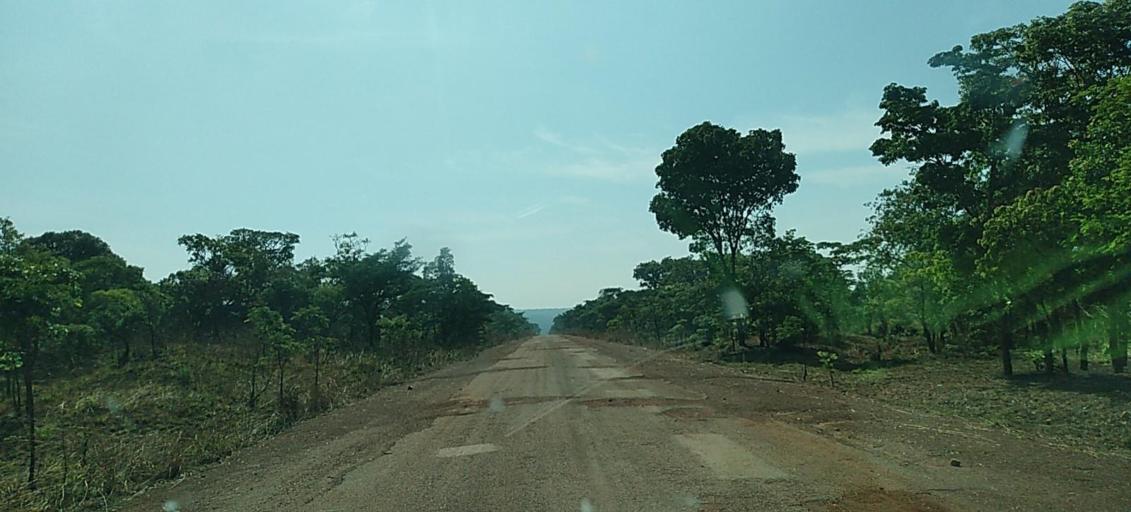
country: ZM
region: North-Western
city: Mwinilunga
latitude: -11.8219
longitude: 25.1032
